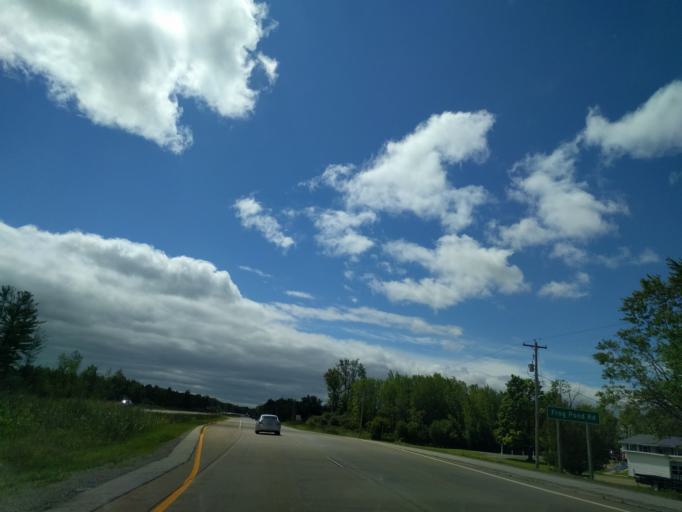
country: US
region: Wisconsin
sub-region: Oconto County
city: Oconto
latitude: 44.8652
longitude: -87.8994
